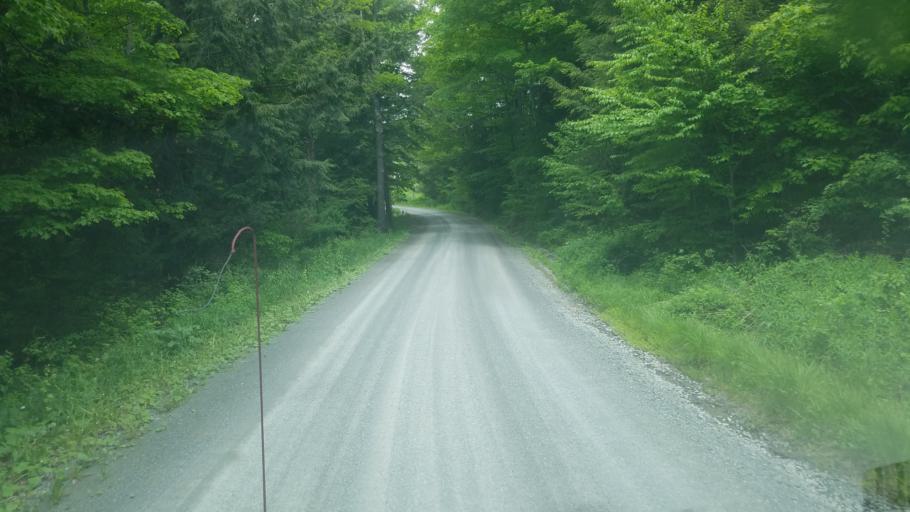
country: US
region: Pennsylvania
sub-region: Tioga County
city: Westfield
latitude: 41.8498
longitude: -77.6035
